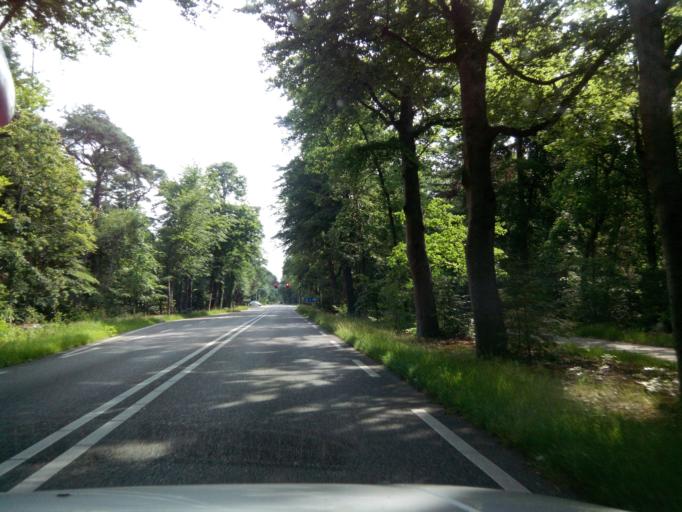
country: NL
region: Utrecht
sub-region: Gemeente Zeist
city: Zeist
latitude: 52.0867
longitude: 5.2617
